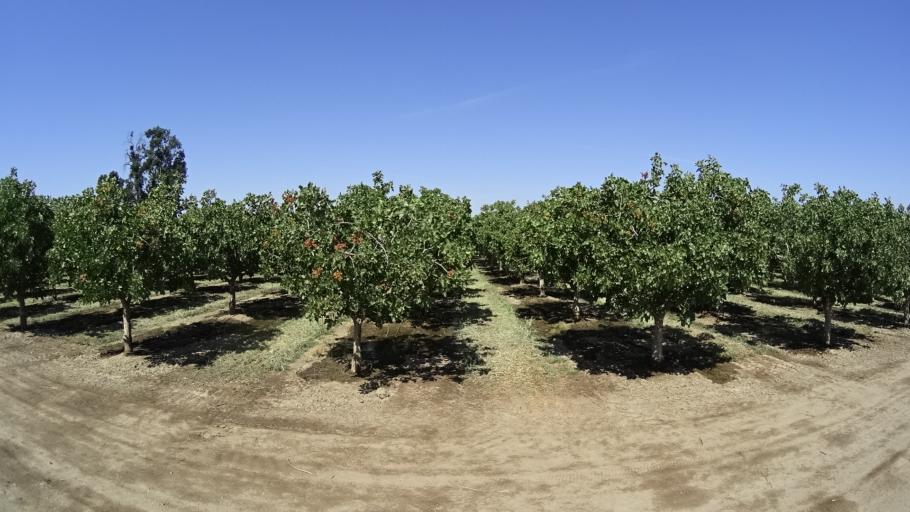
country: US
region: California
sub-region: Kings County
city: Lemoore
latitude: 36.3482
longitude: -119.8250
